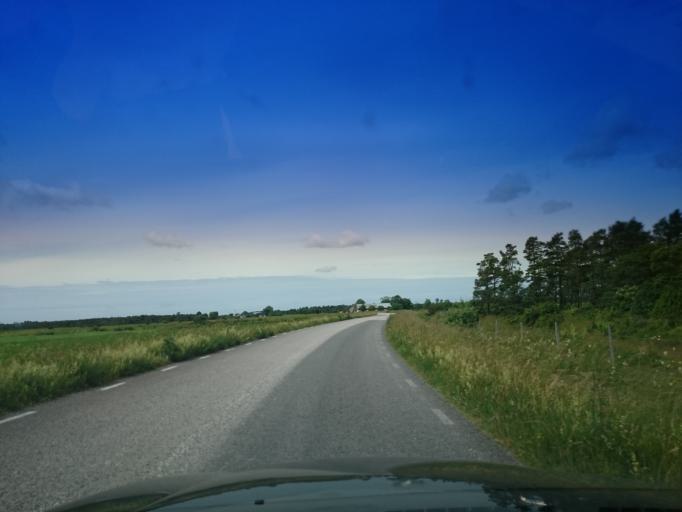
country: SE
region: Gotland
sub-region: Gotland
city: Hemse
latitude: 57.2527
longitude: 18.5794
